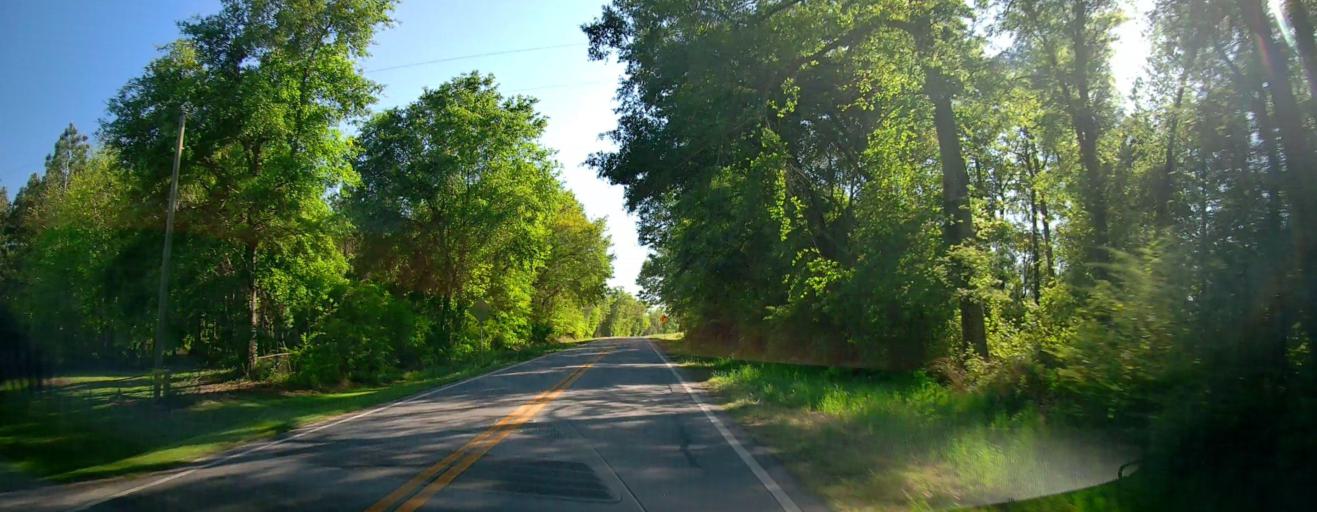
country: US
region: Georgia
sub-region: Wilcox County
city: Rochelle
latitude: 31.9077
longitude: -83.4815
